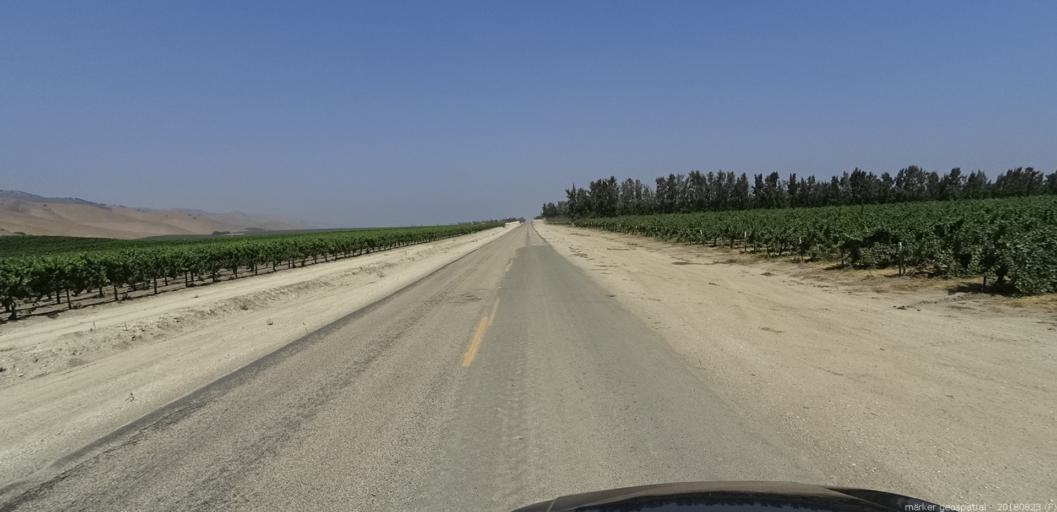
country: US
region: California
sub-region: Monterey County
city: King City
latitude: 36.2421
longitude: -121.1868
